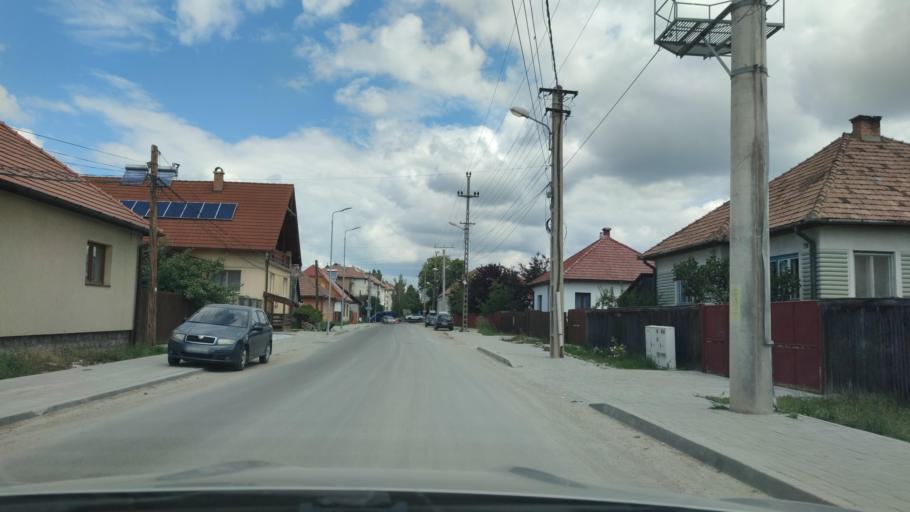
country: RO
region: Harghita
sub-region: Municipiul Gheorgheni
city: Gheorgheni
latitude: 46.7172
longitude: 25.5909
